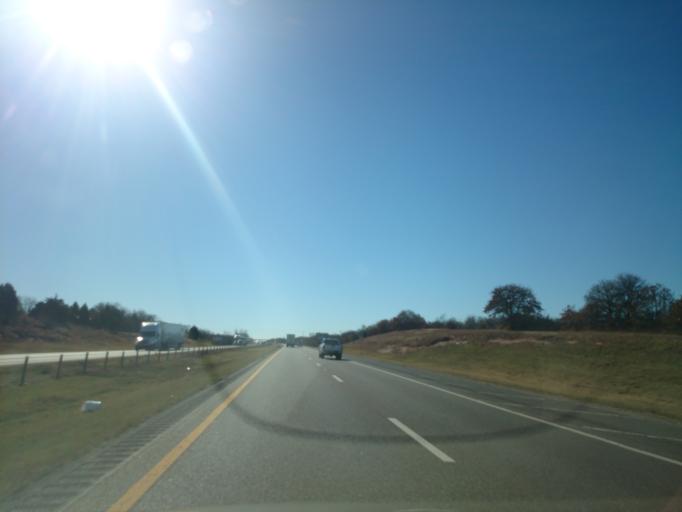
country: US
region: Oklahoma
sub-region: Oklahoma County
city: Edmond
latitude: 35.6761
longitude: -97.4184
